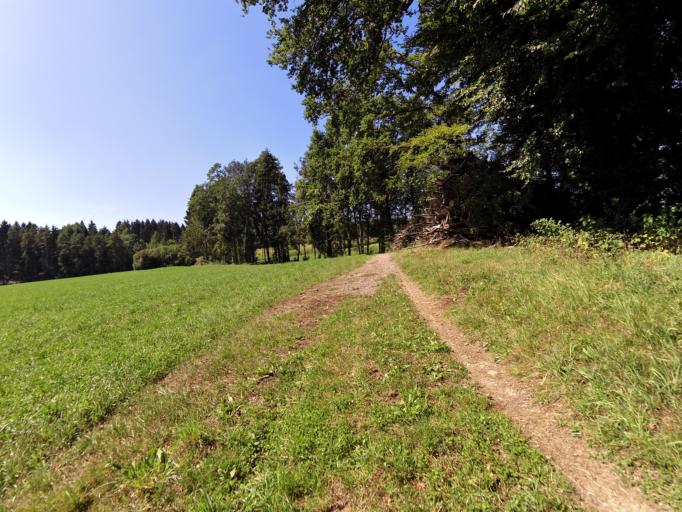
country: CH
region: Thurgau
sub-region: Kreuzlingen District
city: Tagerwilen
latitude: 47.6400
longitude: 9.1320
